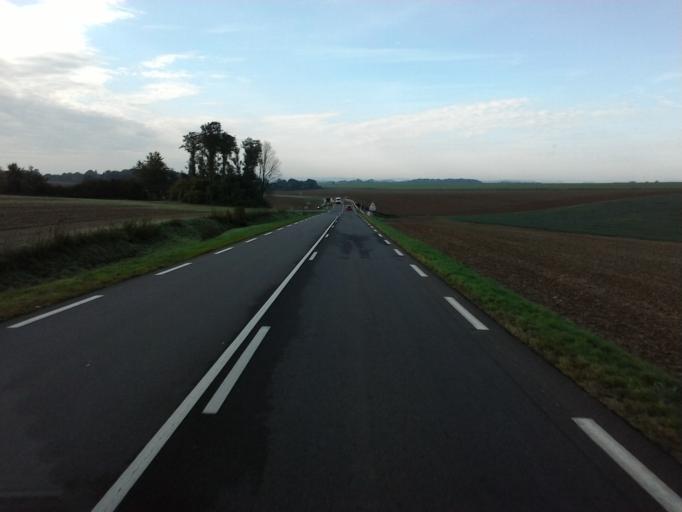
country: FR
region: Lorraine
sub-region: Departement de Meurthe-et-Moselle
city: Longuyon
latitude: 49.4738
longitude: 5.5984
